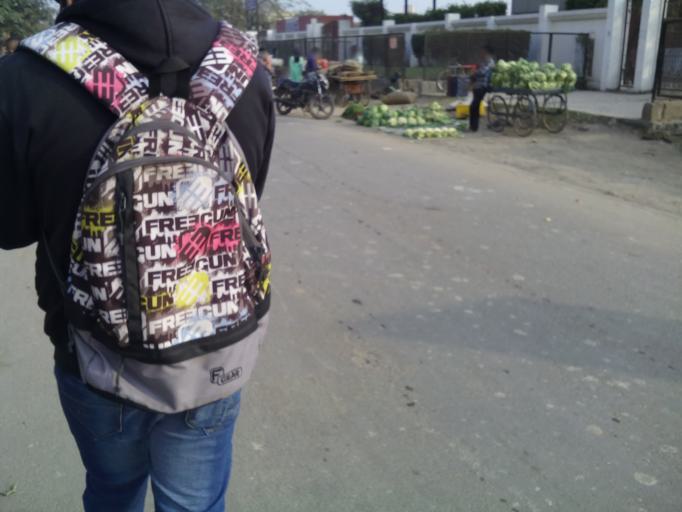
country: IN
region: Uttar Pradesh
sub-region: Kanpur
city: Kanpur
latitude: 26.4340
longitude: 80.3090
